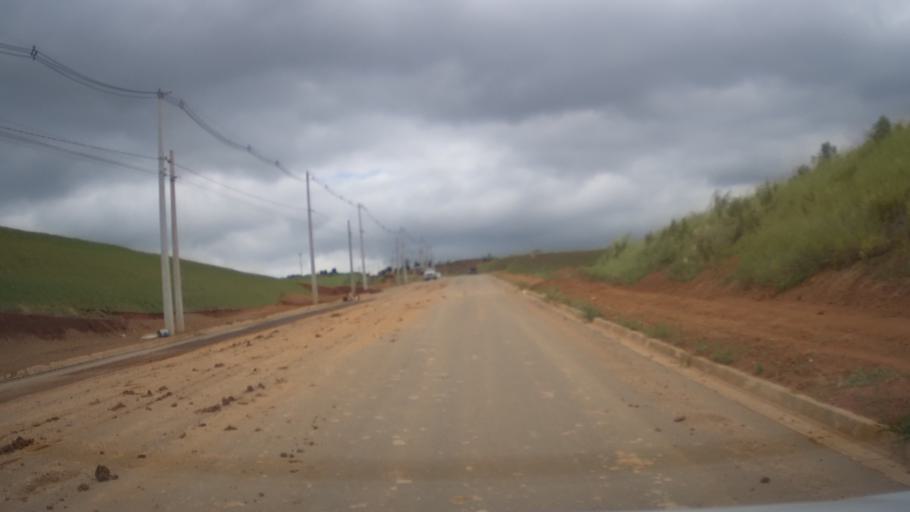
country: BR
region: Sao Paulo
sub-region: Vinhedo
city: Vinhedo
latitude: -23.0745
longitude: -47.0070
